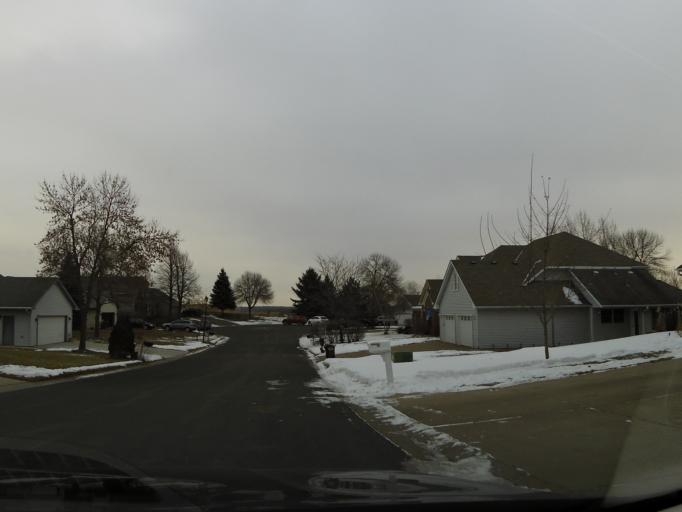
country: US
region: Minnesota
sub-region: Carver County
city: Waconia
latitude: 44.8482
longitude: -93.7757
